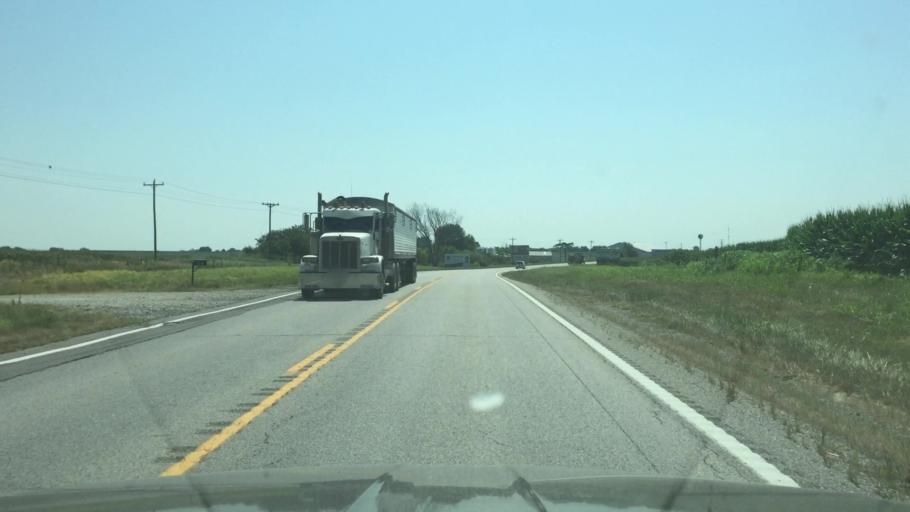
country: US
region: Missouri
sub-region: Moniteau County
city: Tipton
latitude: 38.6629
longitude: -92.8161
